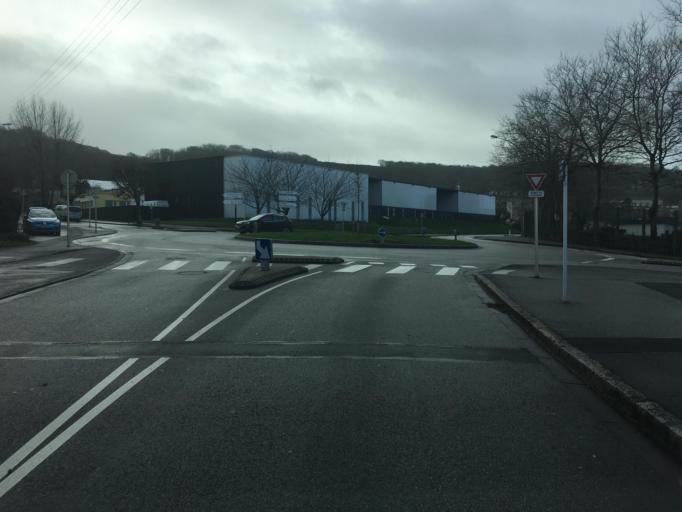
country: FR
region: Lower Normandy
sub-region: Departement de la Manche
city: Cherbourg-Octeville
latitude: 49.6321
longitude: -1.5998
